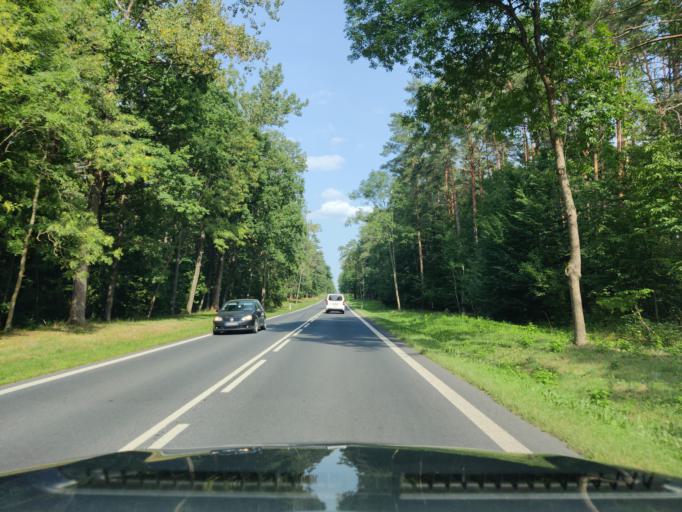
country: PL
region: Masovian Voivodeship
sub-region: Powiat makowski
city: Rzewnie
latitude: 52.8529
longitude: 21.2936
